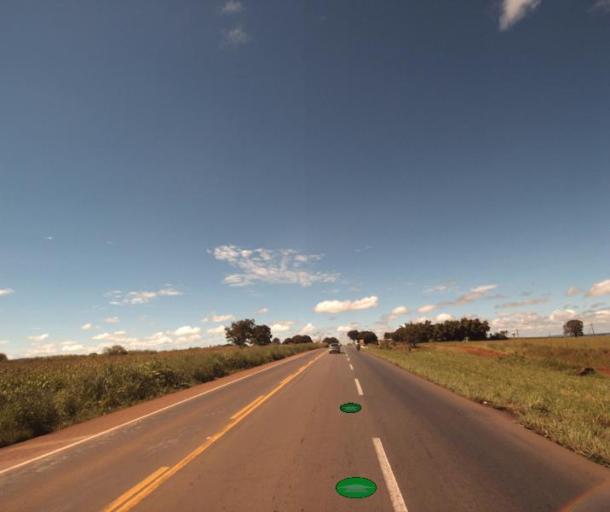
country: BR
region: Goias
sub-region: Rialma
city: Rialma
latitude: -15.3560
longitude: -49.5657
